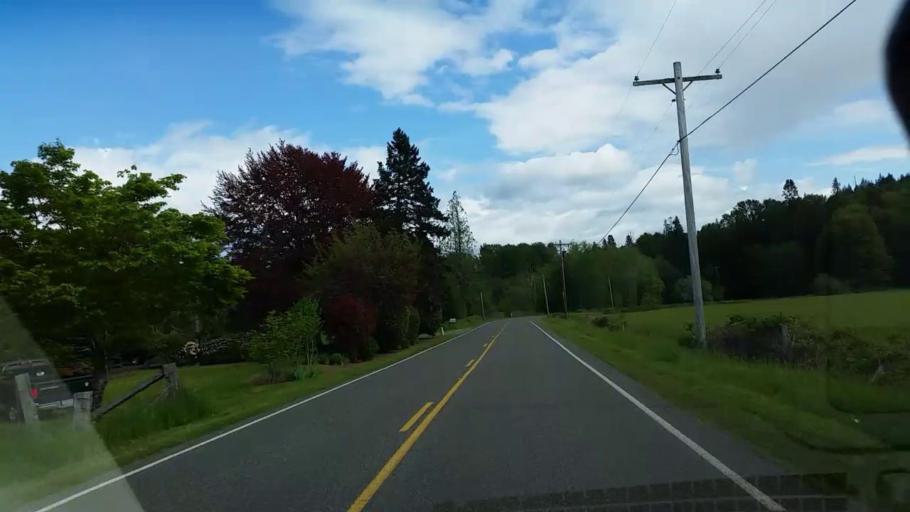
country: US
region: Washington
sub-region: Mason County
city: Shelton
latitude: 47.3182
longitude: -123.2594
